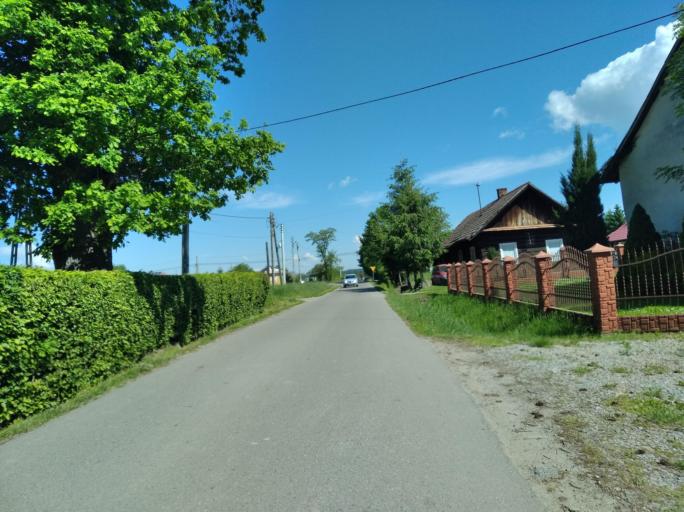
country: PL
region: Subcarpathian Voivodeship
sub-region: Powiat krosnienski
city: Odrzykon
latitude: 49.7369
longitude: 21.7314
